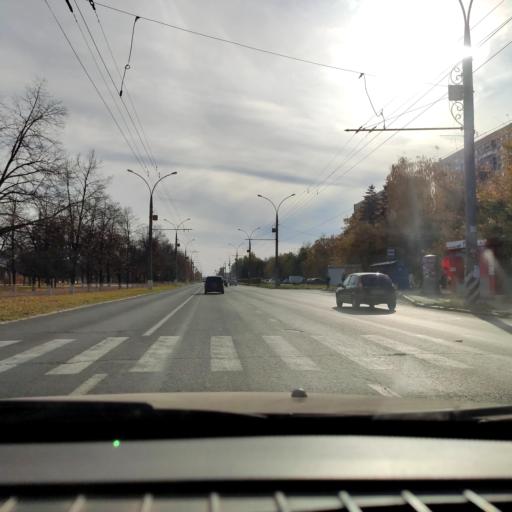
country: RU
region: Samara
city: Tol'yatti
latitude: 53.5251
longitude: 49.2744
